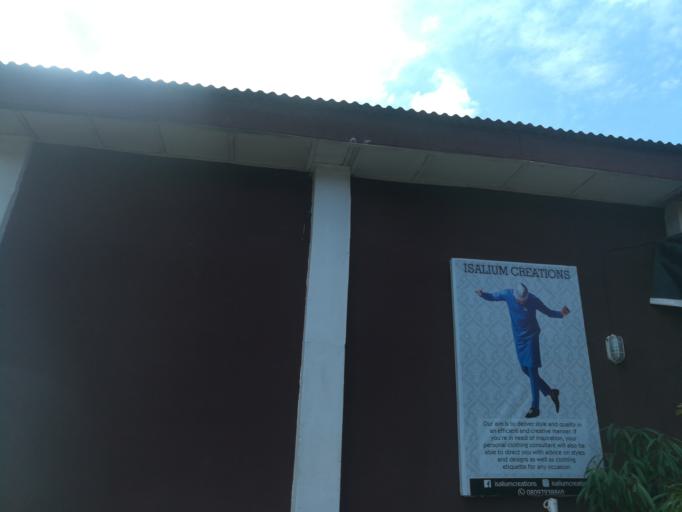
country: NG
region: Lagos
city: Oshodi
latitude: 6.5649
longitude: 3.3342
